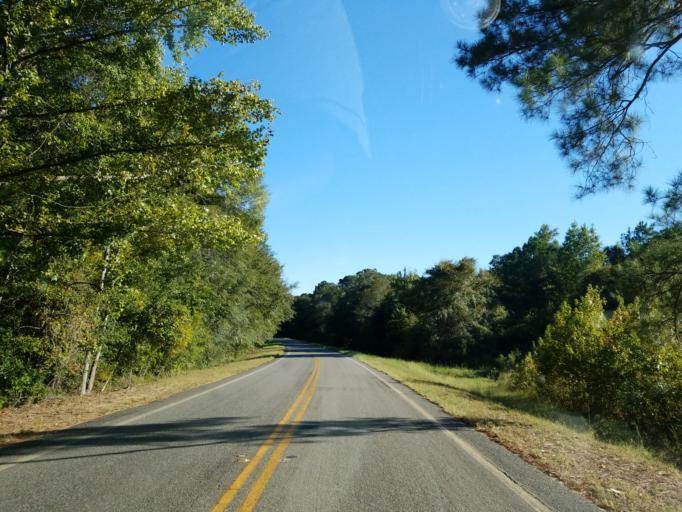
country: US
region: Georgia
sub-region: Dooly County
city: Vienna
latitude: 32.0817
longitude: -83.9595
